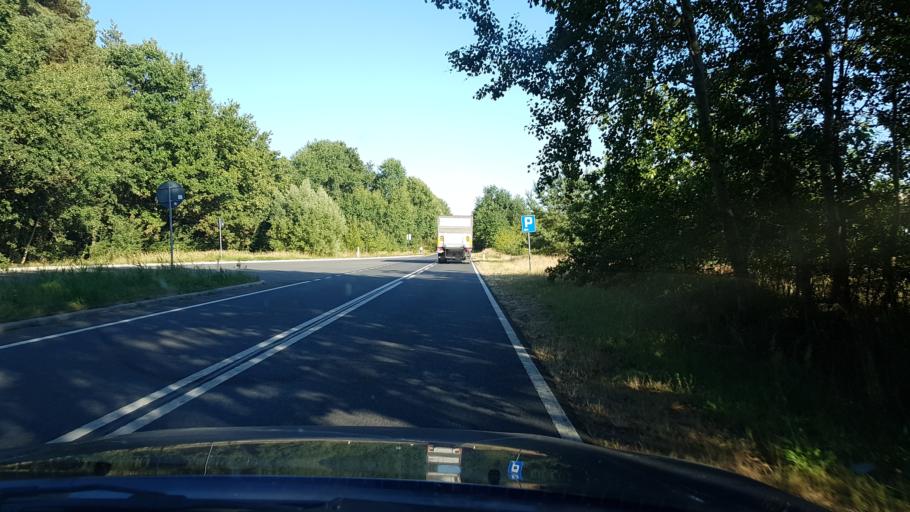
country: PL
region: West Pomeranian Voivodeship
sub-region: Powiat stargardzki
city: Stara Dabrowa
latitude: 53.4325
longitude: 15.2110
